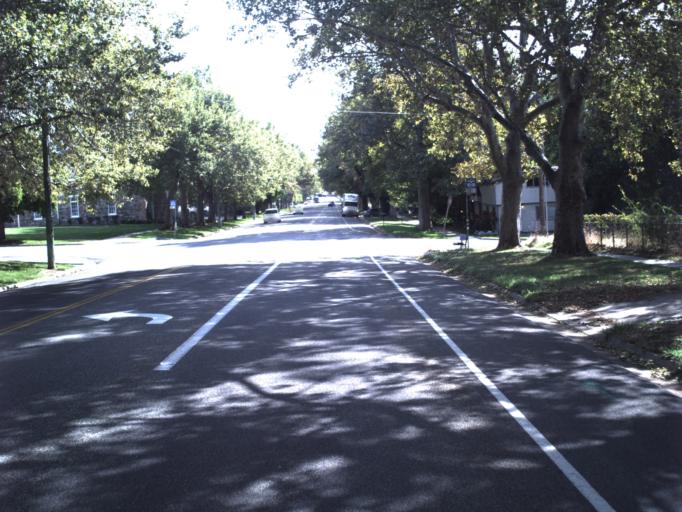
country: US
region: Utah
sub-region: Davis County
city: Farmington
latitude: 40.9859
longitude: -111.8876
